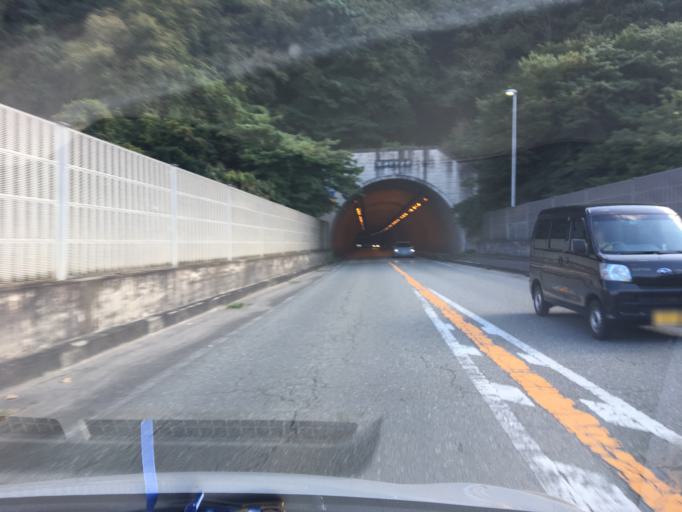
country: JP
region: Hyogo
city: Toyooka
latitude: 35.4652
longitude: 134.7682
